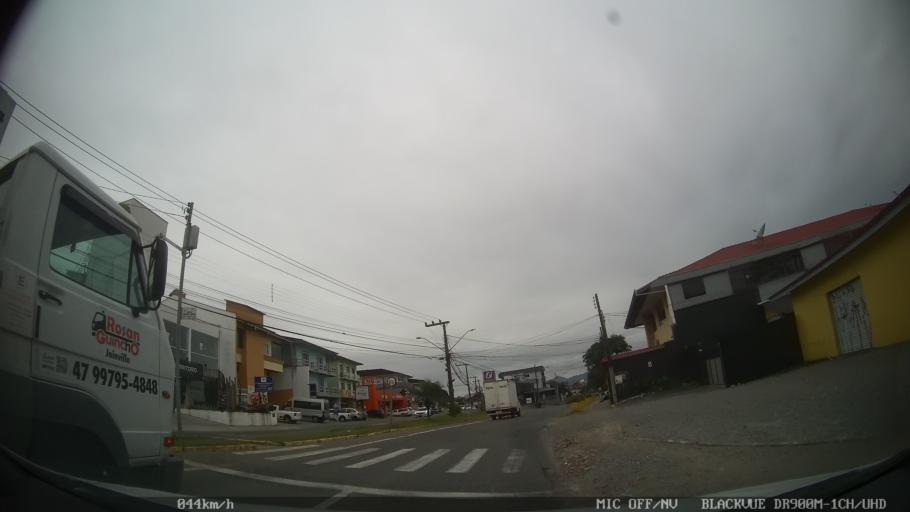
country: BR
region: Santa Catarina
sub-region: Joinville
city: Joinville
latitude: -26.2671
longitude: -48.8220
